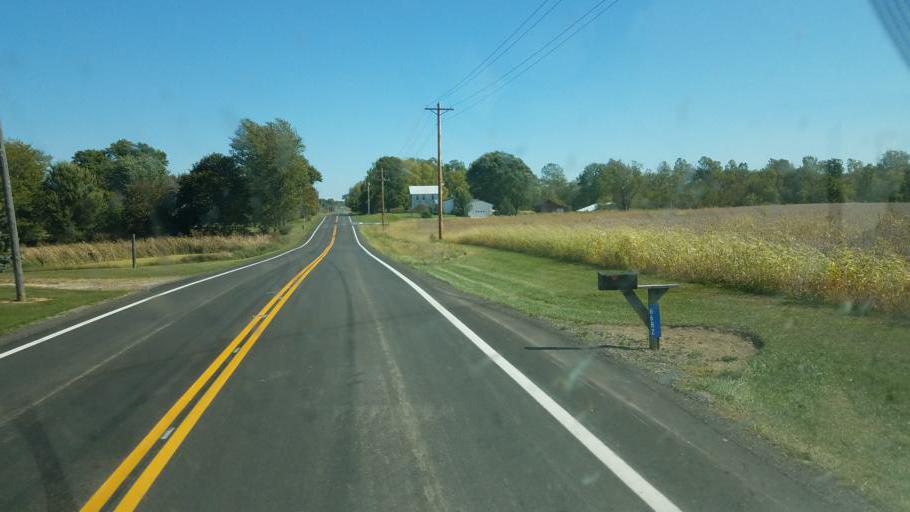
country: US
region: Ohio
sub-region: Huron County
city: Willard
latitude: 40.9601
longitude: -82.7941
